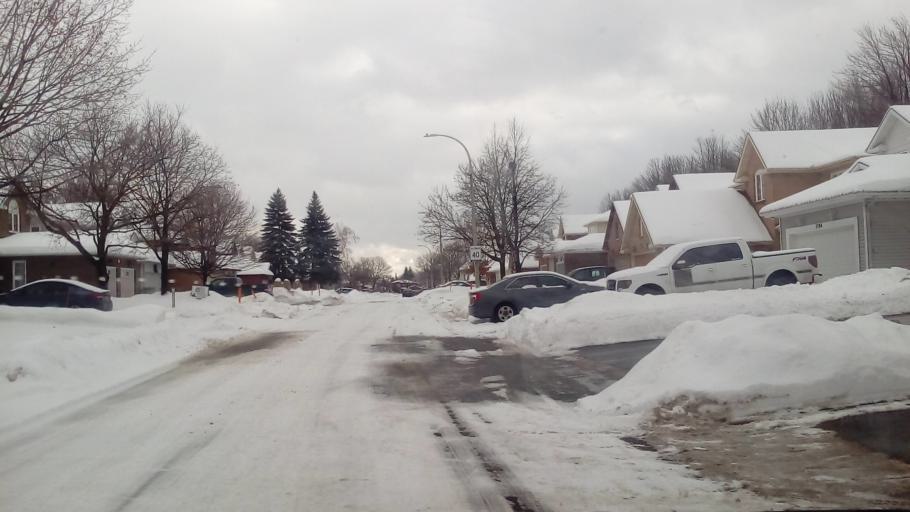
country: CA
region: Quebec
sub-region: Outaouais
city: Gatineau
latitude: 45.4588
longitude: -75.5297
